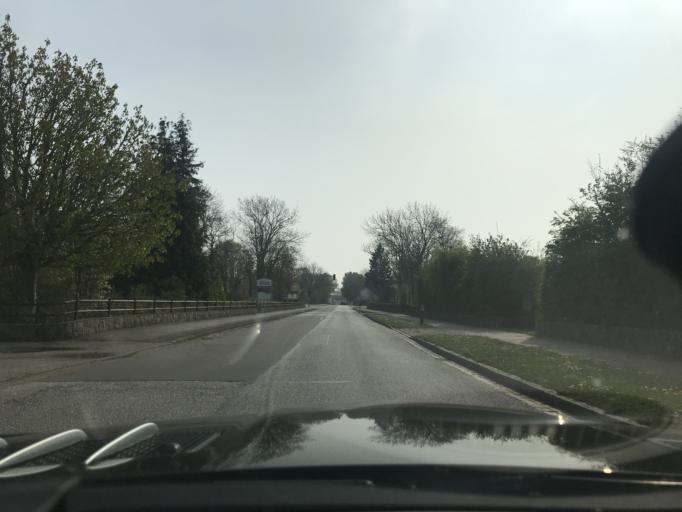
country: DE
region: Schleswig-Holstein
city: Fehmarn
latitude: 54.4965
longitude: 11.2129
